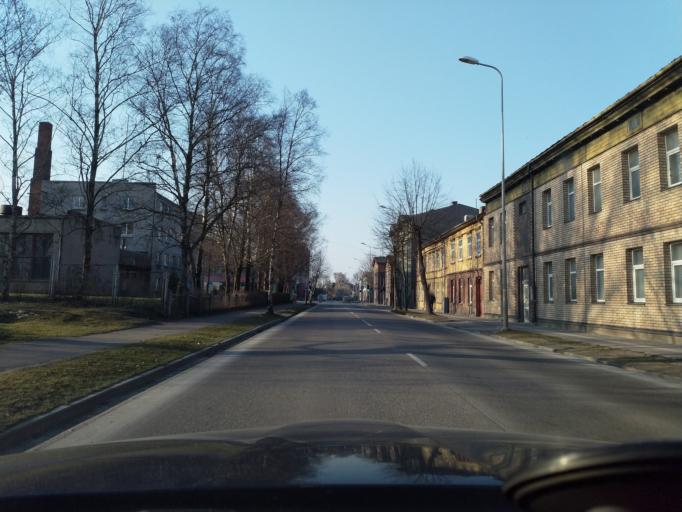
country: LV
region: Liepaja
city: Liepaja
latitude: 56.5037
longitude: 21.0192
